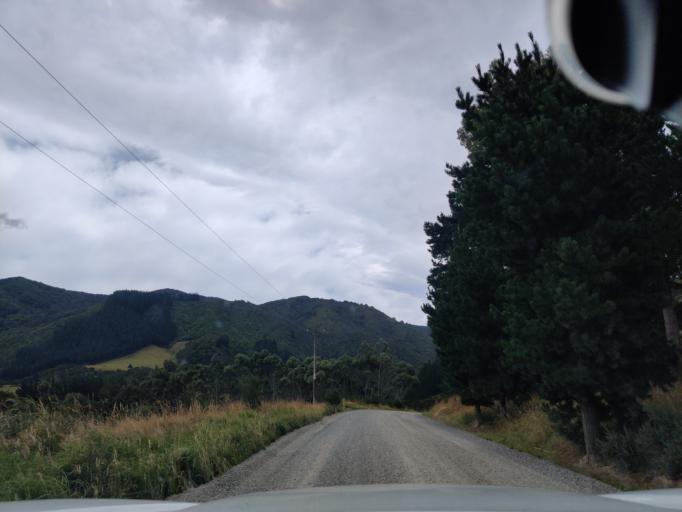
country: NZ
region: Wellington
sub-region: Masterton District
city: Masterton
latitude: -41.0368
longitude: 175.4008
